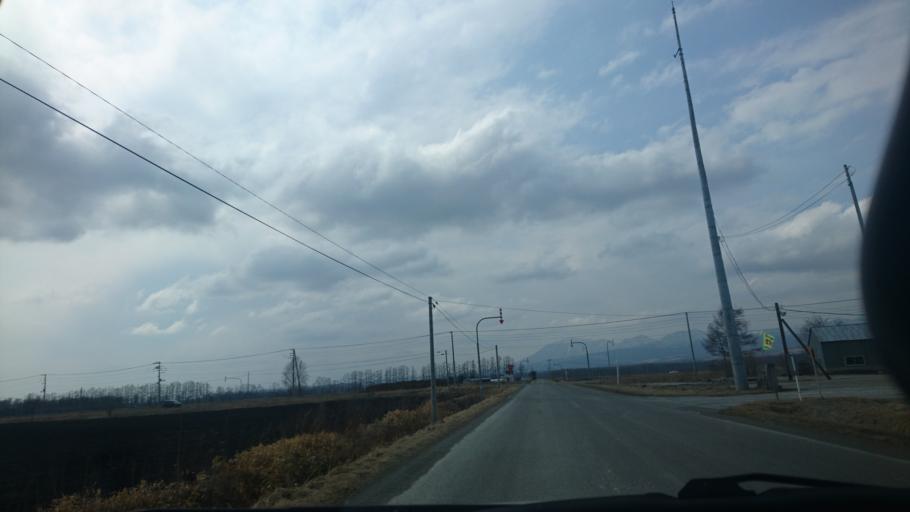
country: JP
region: Hokkaido
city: Otofuke
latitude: 43.2163
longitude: 143.2819
